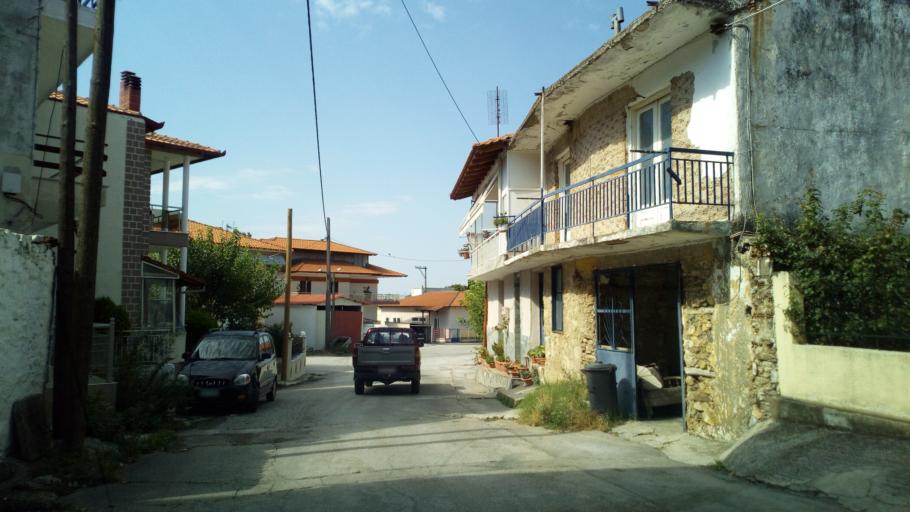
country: GR
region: Central Macedonia
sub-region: Nomos Thessalonikis
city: Sochos
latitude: 40.8165
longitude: 23.3546
